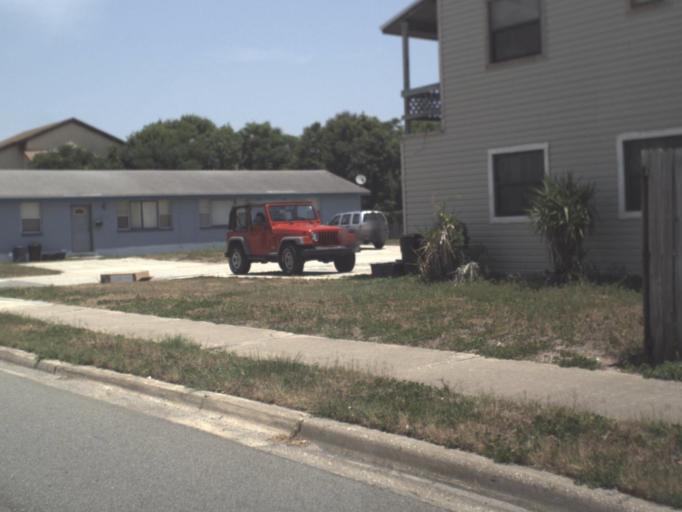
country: US
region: Florida
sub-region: Duval County
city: Neptune Beach
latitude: 30.3181
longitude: -81.3972
